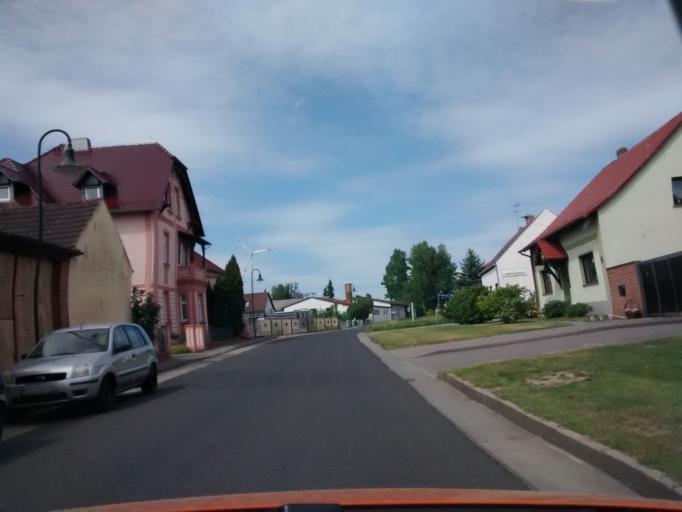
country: DE
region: Brandenburg
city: Ihlow
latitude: 51.8912
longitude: 13.3051
